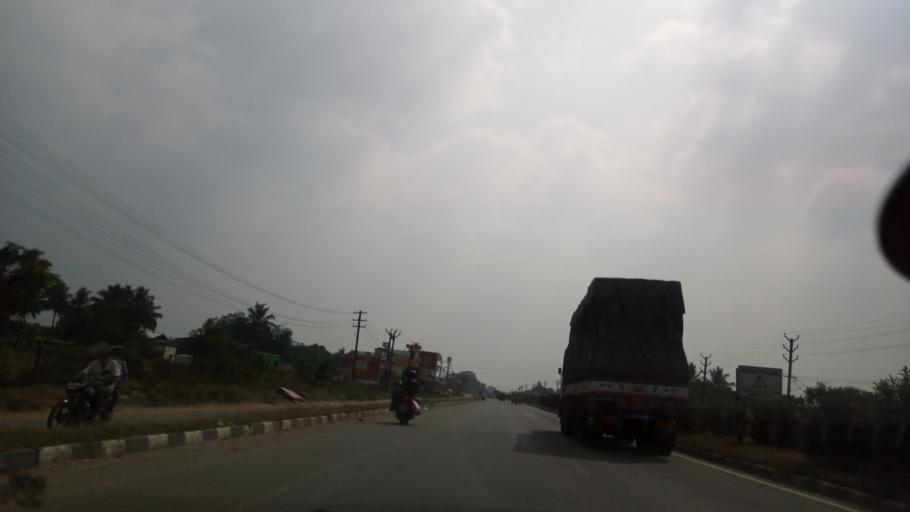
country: IN
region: Tamil Nadu
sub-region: Salem
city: Omalur
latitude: 11.7685
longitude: 78.0535
